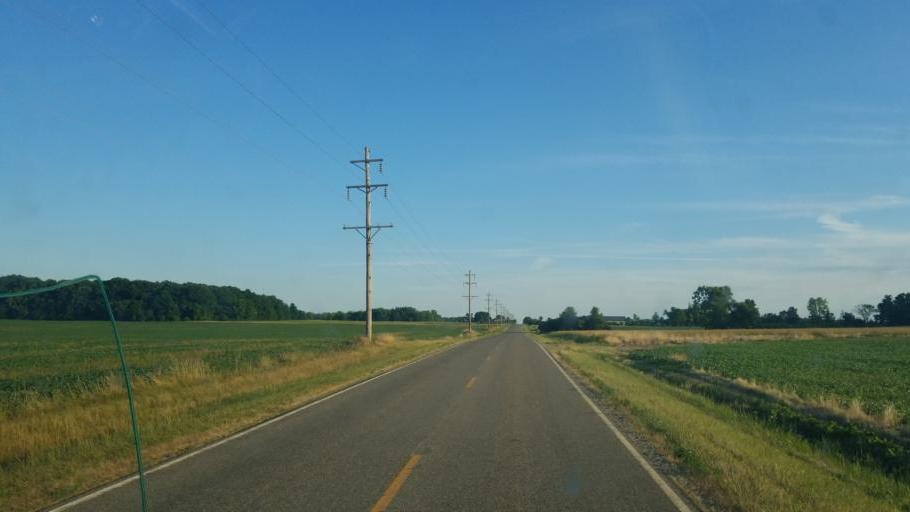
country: US
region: Ohio
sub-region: Williams County
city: Edgerton
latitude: 41.3794
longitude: -84.7671
